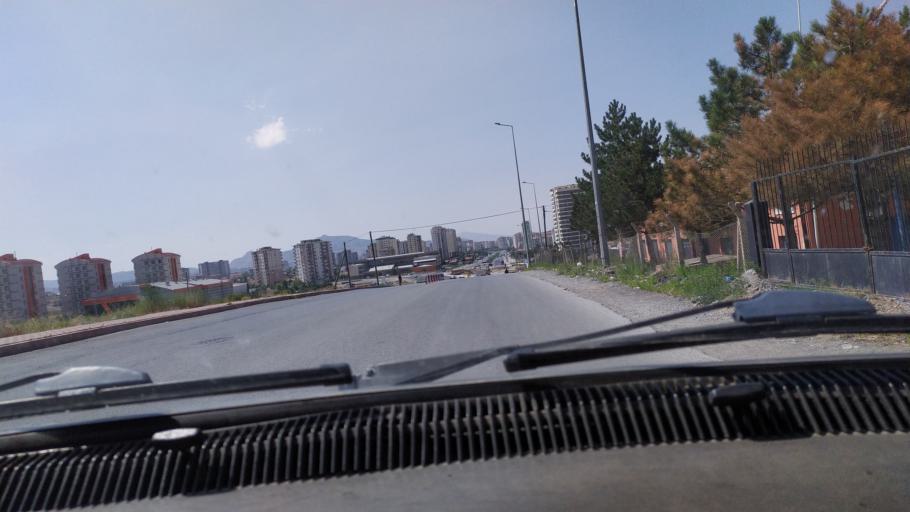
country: TR
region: Kayseri
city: Talas
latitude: 38.7198
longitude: 35.5536
